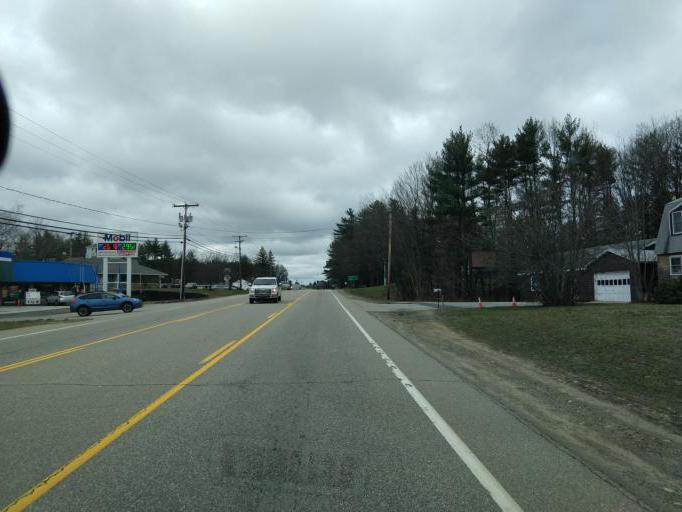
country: US
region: New Hampshire
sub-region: Strafford County
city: Rochester
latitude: 43.3239
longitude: -71.0006
